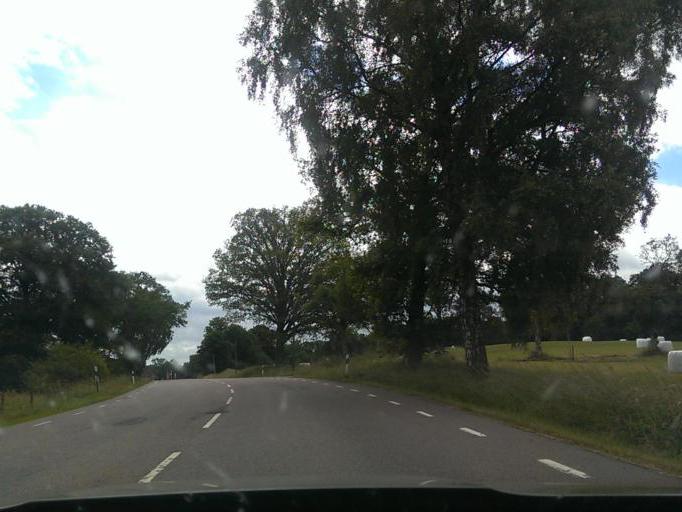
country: SE
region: Skane
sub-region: Klippans Kommun
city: Ljungbyhed
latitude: 56.0073
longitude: 13.2851
